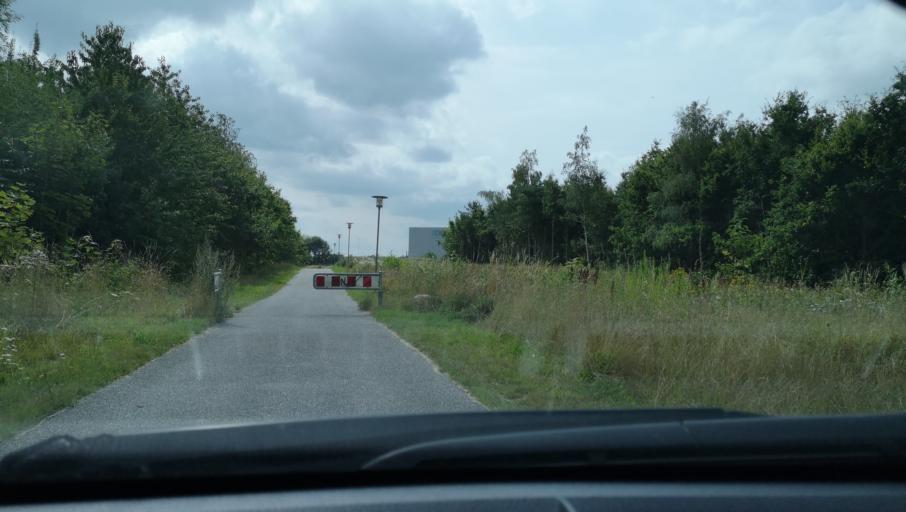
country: DK
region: Zealand
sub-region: Solrod Kommune
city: Solrod
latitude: 55.4977
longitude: 12.1656
